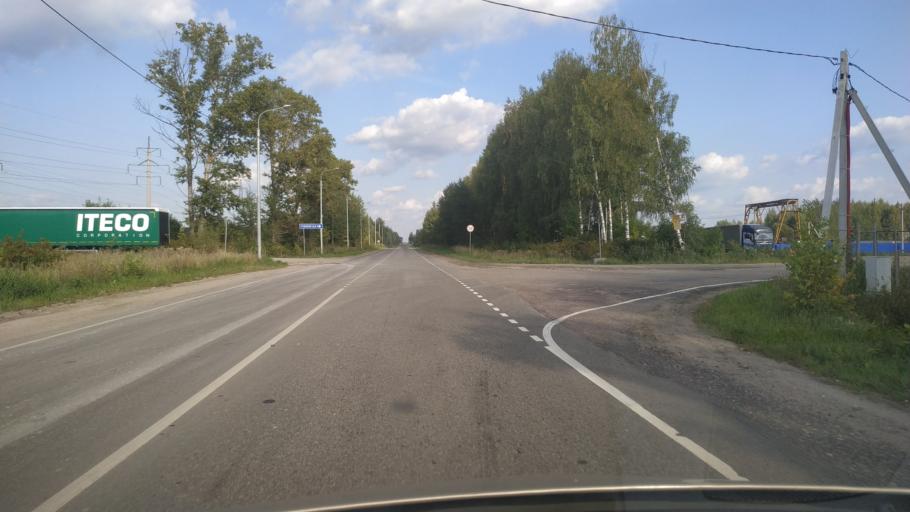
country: RU
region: Moskovskaya
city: Vereya
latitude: 55.7086
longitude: 39.0932
